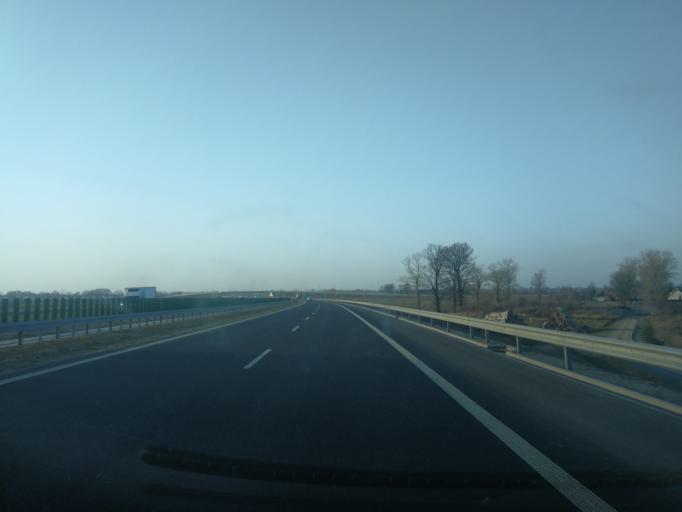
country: PL
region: Pomeranian Voivodeship
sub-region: Powiat nowodworski
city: Nowy Dwor Gdanski
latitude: 54.1825
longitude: 19.1789
